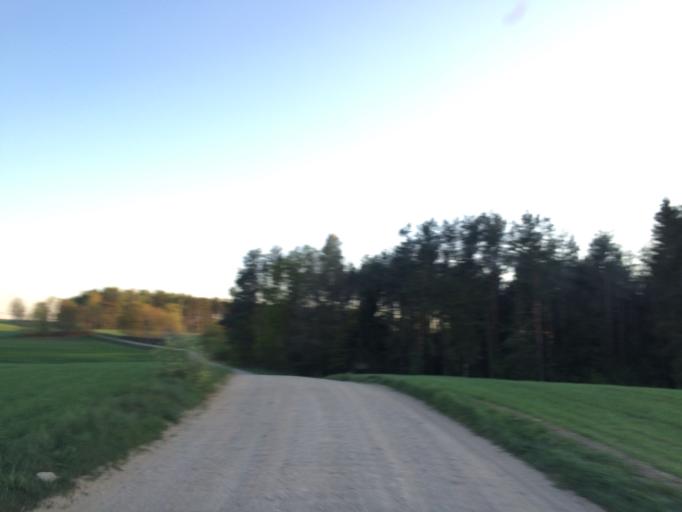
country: PL
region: Warmian-Masurian Voivodeship
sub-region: Powiat dzialdowski
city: Rybno
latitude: 53.4656
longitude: 19.9069
